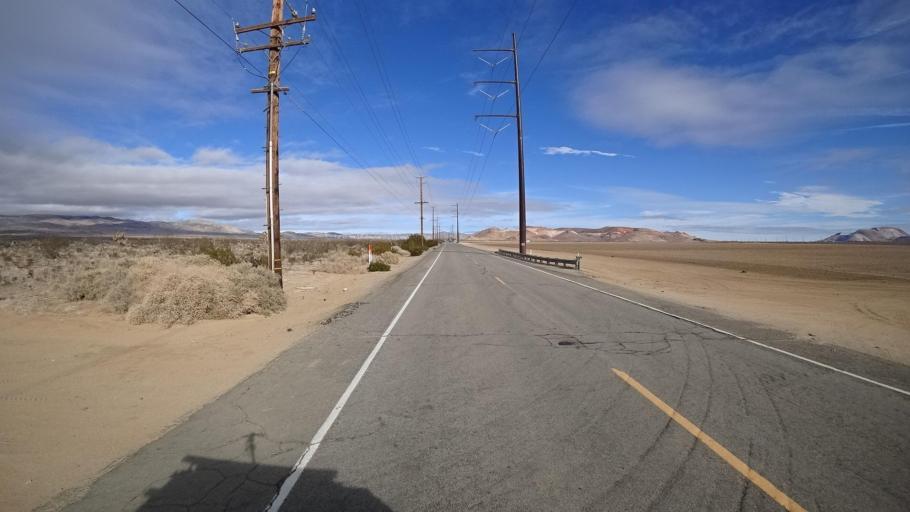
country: US
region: California
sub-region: Kern County
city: Rosamond
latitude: 34.9296
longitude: -118.2909
